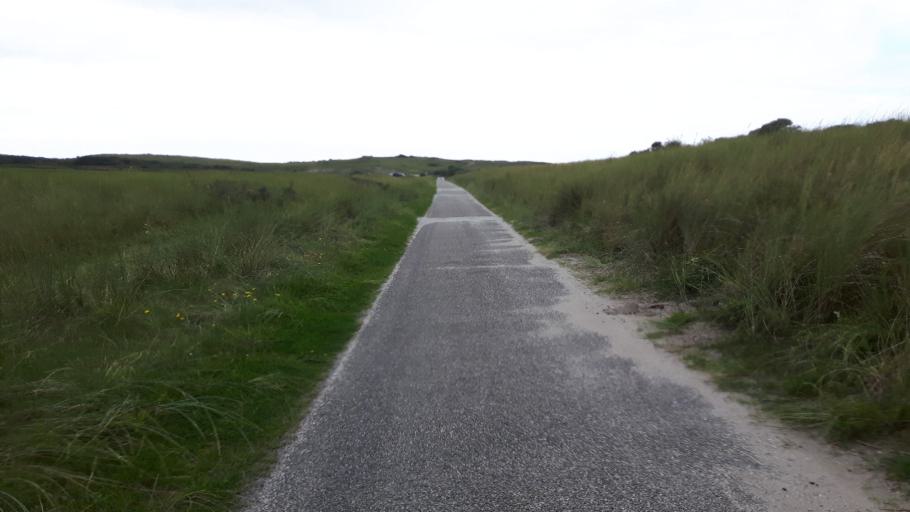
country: NL
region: Friesland
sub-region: Gemeente Ameland
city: Nes
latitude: 53.4611
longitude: 5.8391
